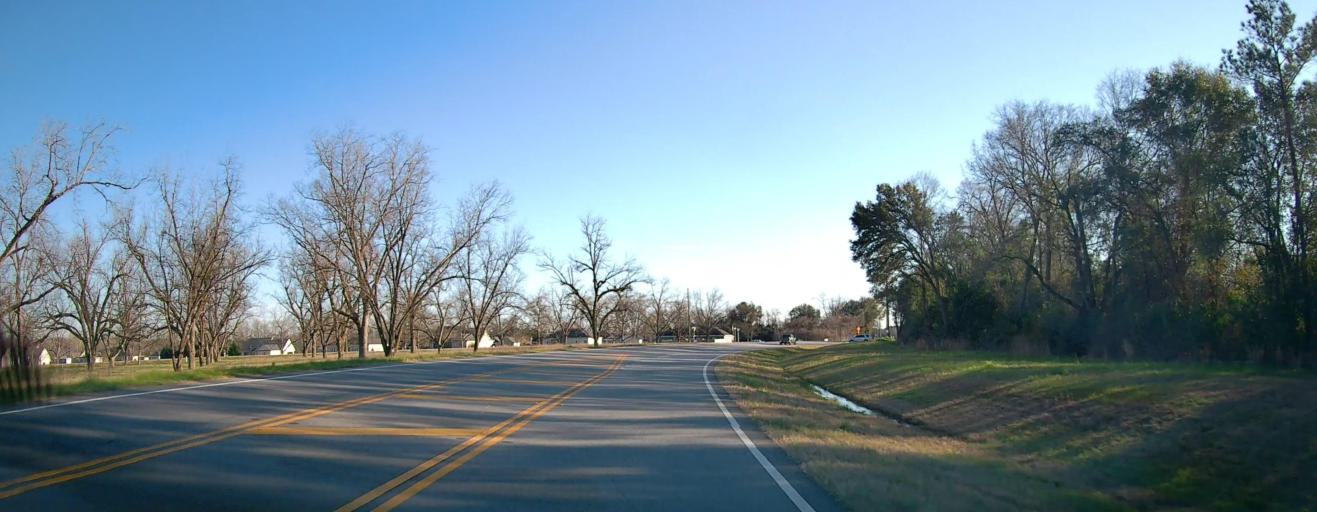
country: US
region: Georgia
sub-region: Dougherty County
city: Albany
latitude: 31.6348
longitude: -84.1629
